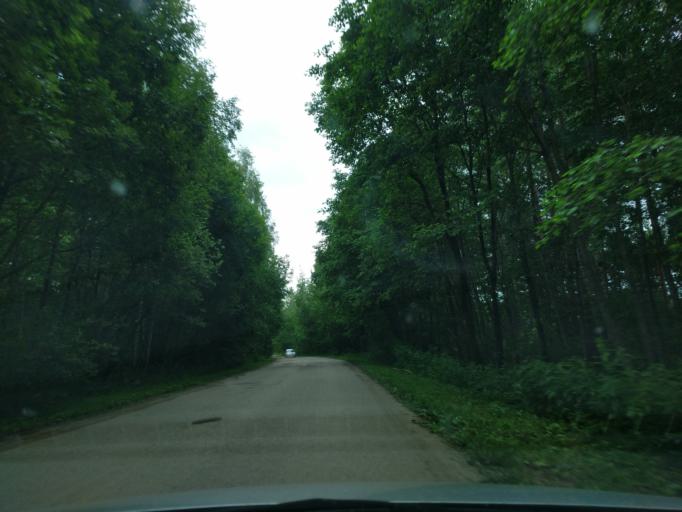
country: RU
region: Kaluga
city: Nikola-Lenivets
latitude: 54.7505
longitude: 35.6673
